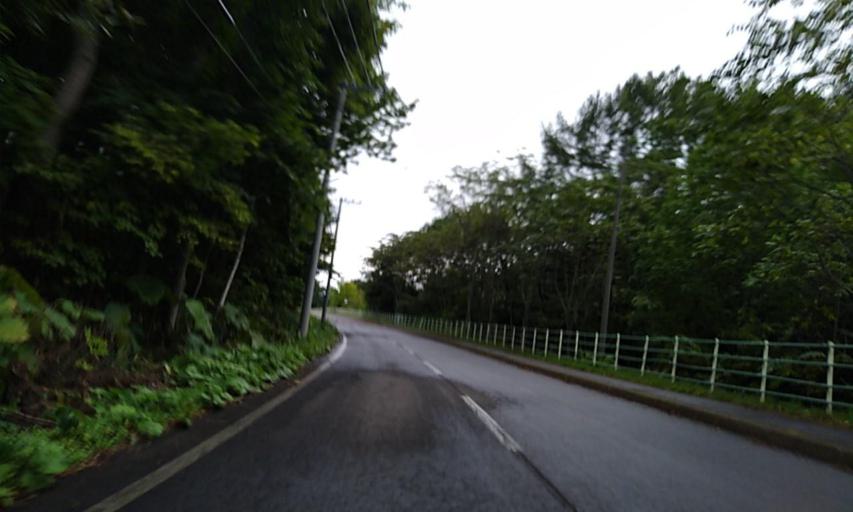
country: JP
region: Hokkaido
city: Abashiri
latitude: 44.0007
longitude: 144.2296
